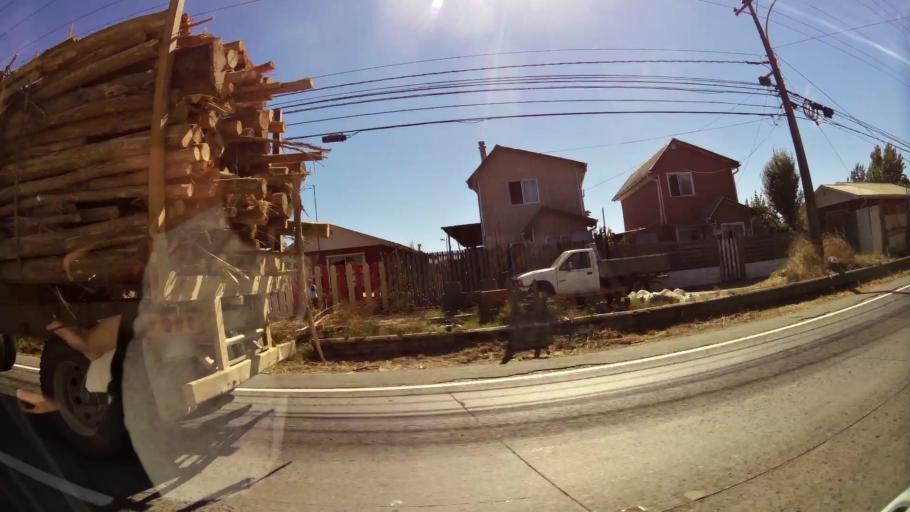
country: CL
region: Biobio
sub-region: Provincia de Concepcion
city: Concepcion
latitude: -36.7958
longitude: -73.0258
